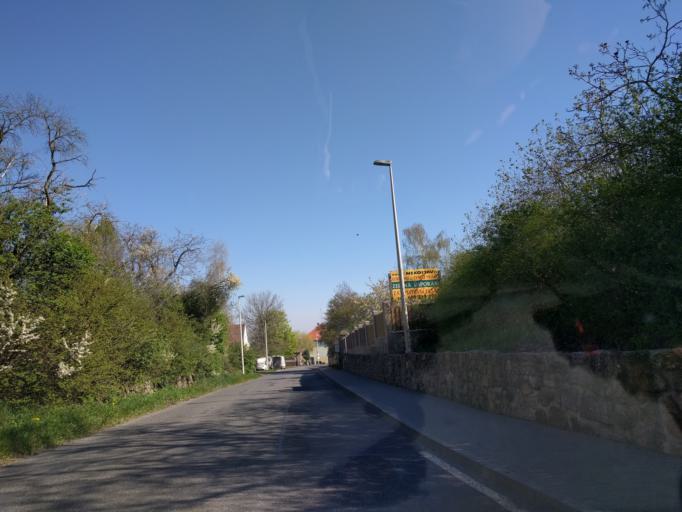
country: CZ
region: Central Bohemia
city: Mukarov
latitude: 50.0215
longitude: 14.7879
